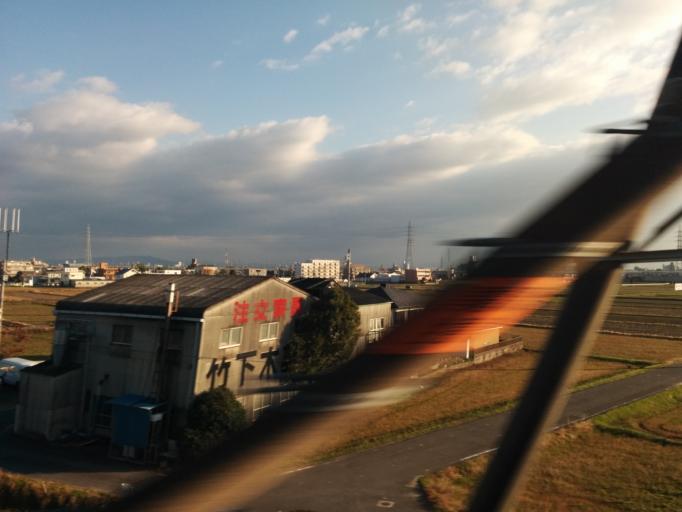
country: JP
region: Aichi
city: Chiryu
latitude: 35.0022
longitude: 137.0199
